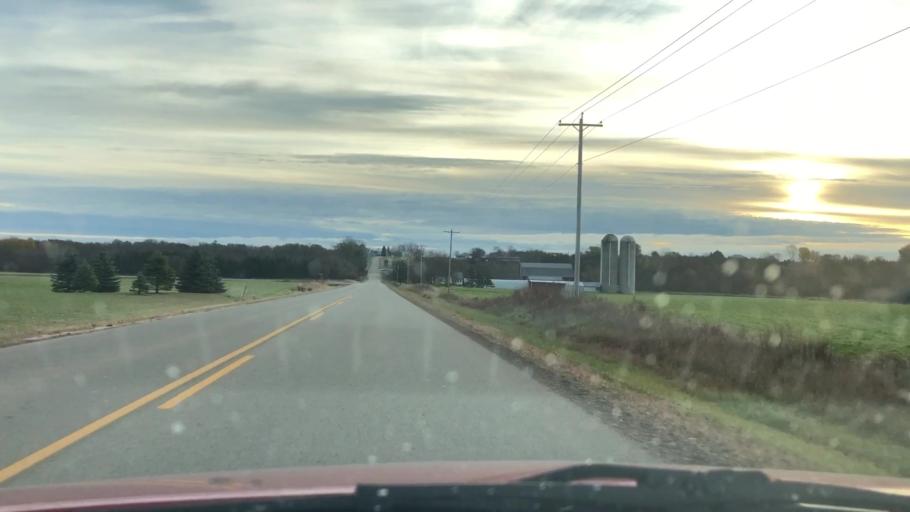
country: US
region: Wisconsin
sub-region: Outagamie County
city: Seymour
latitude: 44.4151
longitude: -88.2687
